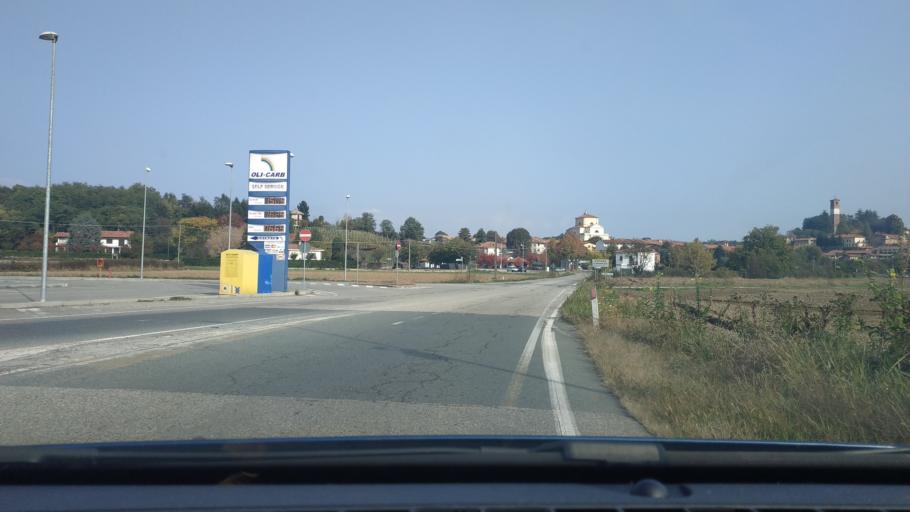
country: IT
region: Piedmont
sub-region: Provincia di Torino
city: Romano Canavese
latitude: 45.3862
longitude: 7.8631
